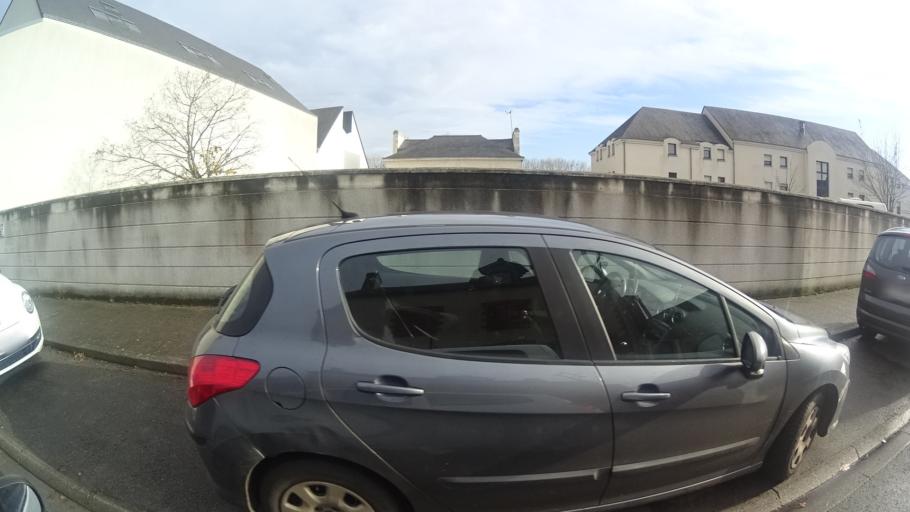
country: FR
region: Brittany
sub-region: Departement d'Ille-et-Vilaine
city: Redon
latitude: 47.6454
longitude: -2.0907
